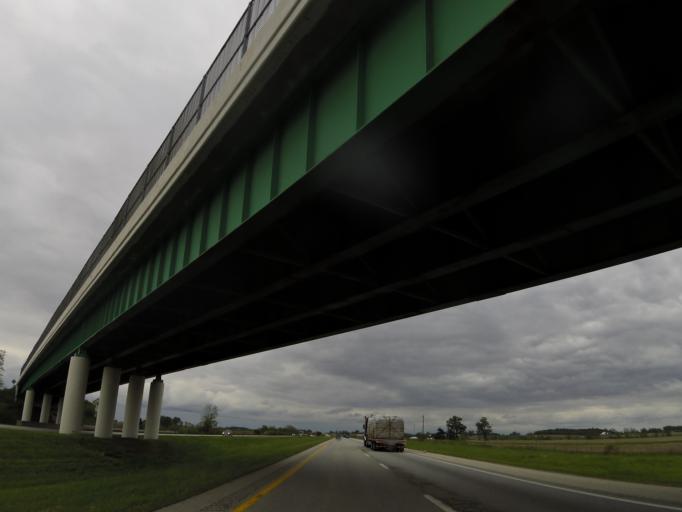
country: US
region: Ohio
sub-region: Greene County
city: Jamestown
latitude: 39.5474
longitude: -83.7473
